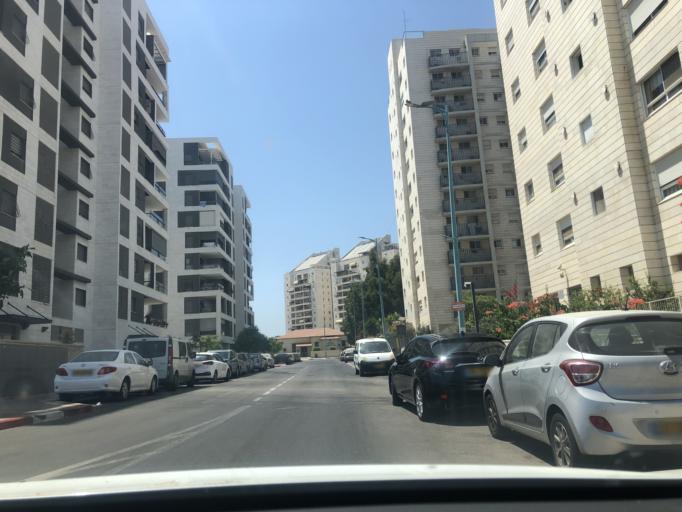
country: IL
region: Central District
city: Lod
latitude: 31.9435
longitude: 34.9025
